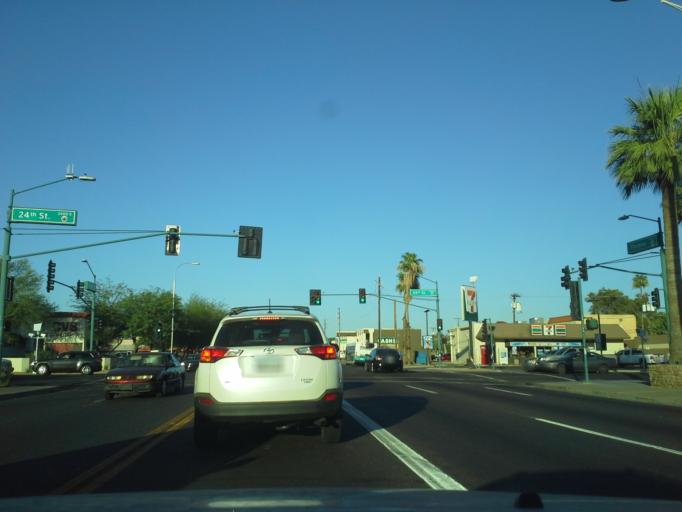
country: US
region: Arizona
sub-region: Maricopa County
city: Phoenix
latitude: 33.4803
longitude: -112.0307
